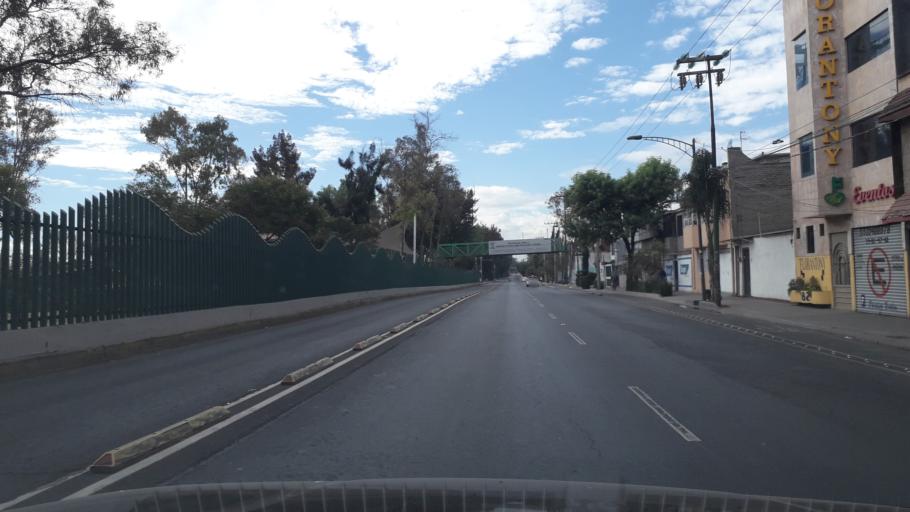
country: MX
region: Mexico City
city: Gustavo A. Madero
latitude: 19.4925
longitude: -99.0924
